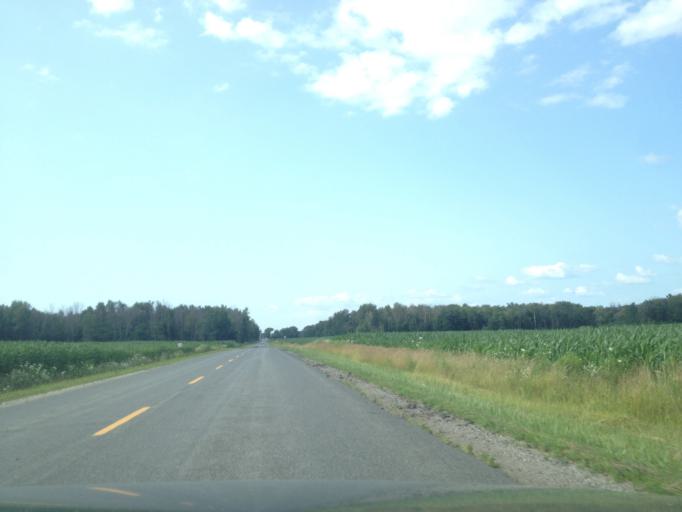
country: CA
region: Ontario
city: Aylmer
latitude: 42.6818
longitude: -80.8597
